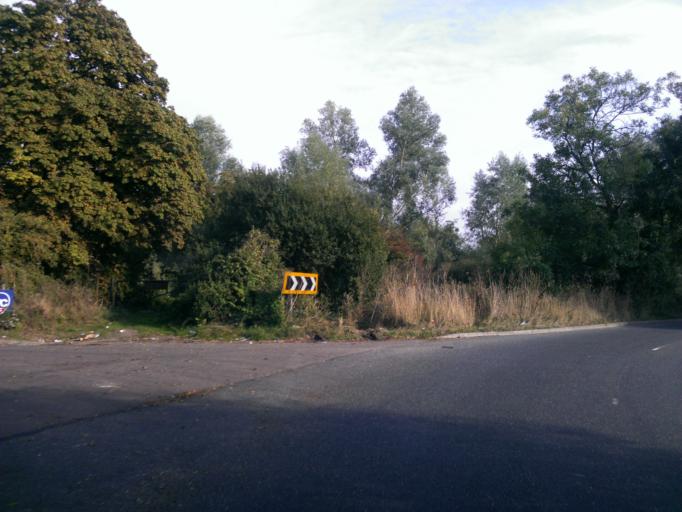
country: GB
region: England
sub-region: Essex
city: Witham
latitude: 51.8112
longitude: 0.6732
